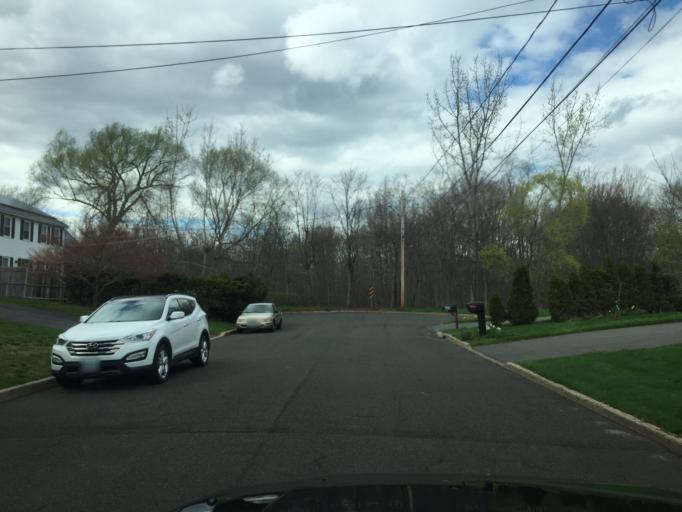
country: US
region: Connecticut
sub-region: Hartford County
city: New Britain
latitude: 41.7006
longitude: -72.7721
